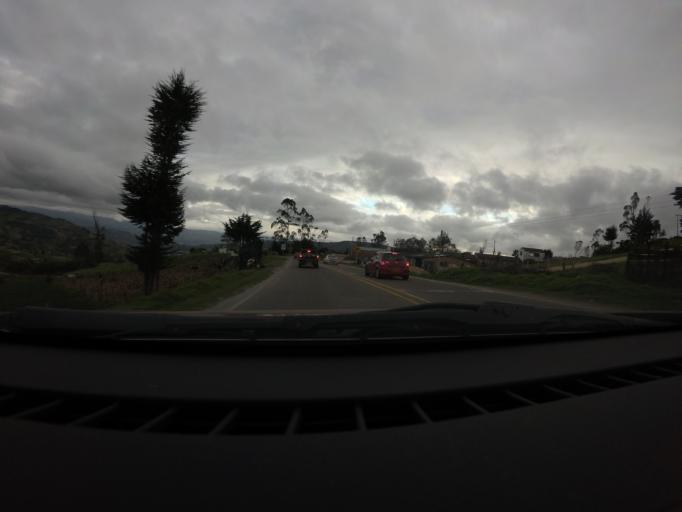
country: CO
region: Boyaca
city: Samaca
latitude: 5.4612
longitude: -73.4176
